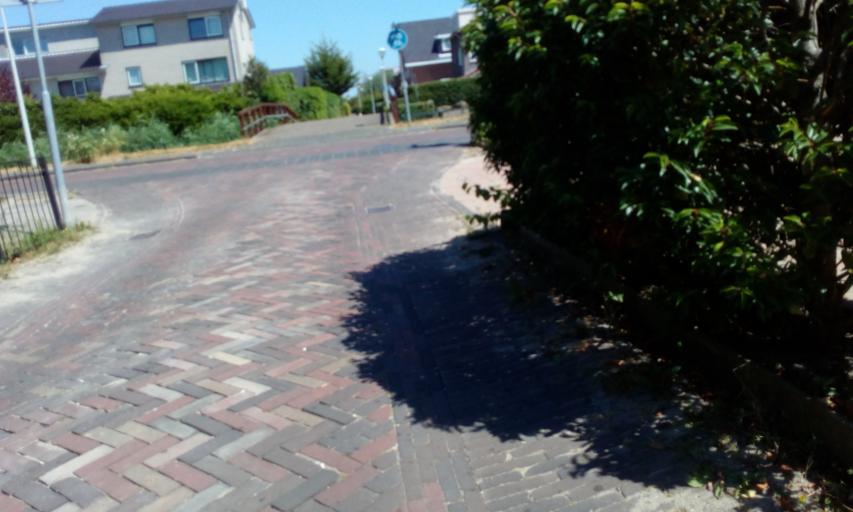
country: NL
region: South Holland
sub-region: Gemeente Den Haag
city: Ypenburg
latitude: 52.0367
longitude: 4.3858
